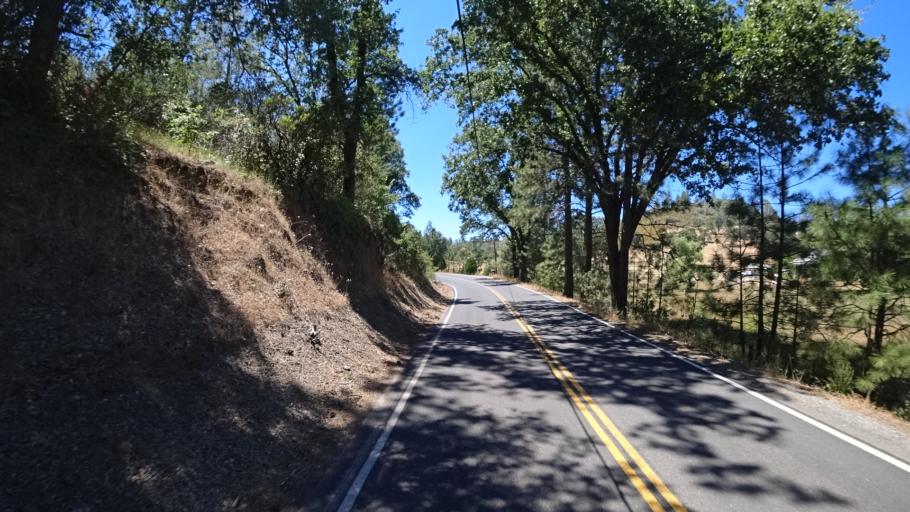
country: US
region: California
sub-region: Calaveras County
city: Mountain Ranch
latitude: 38.2869
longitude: -120.4979
